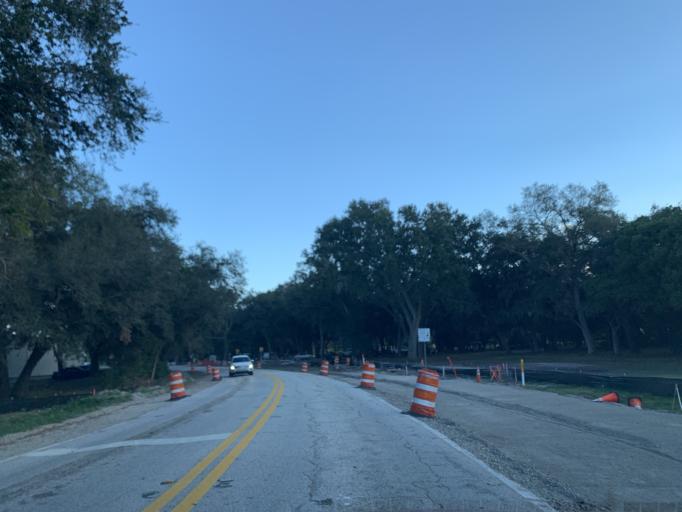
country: US
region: Florida
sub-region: Pinellas County
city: Safety Harbor
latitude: 27.9773
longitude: -82.7378
